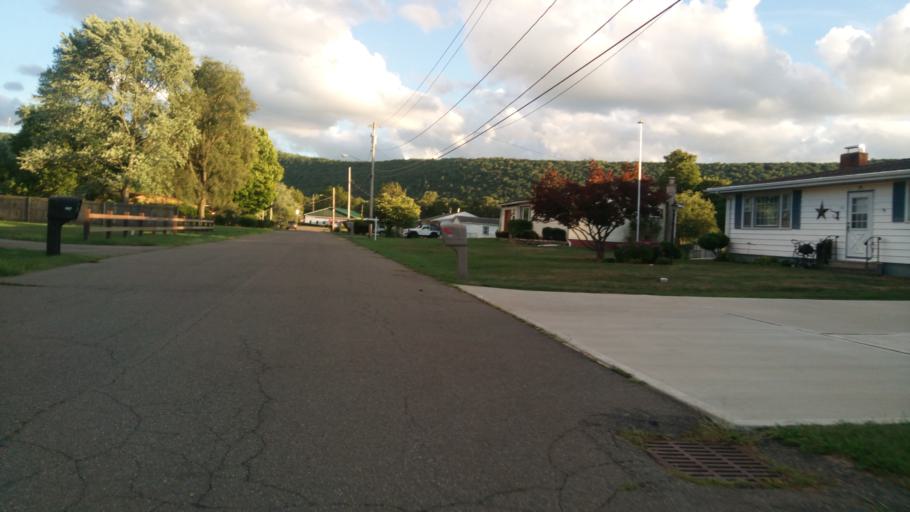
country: US
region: New York
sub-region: Chemung County
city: Southport
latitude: 42.0596
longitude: -76.8004
